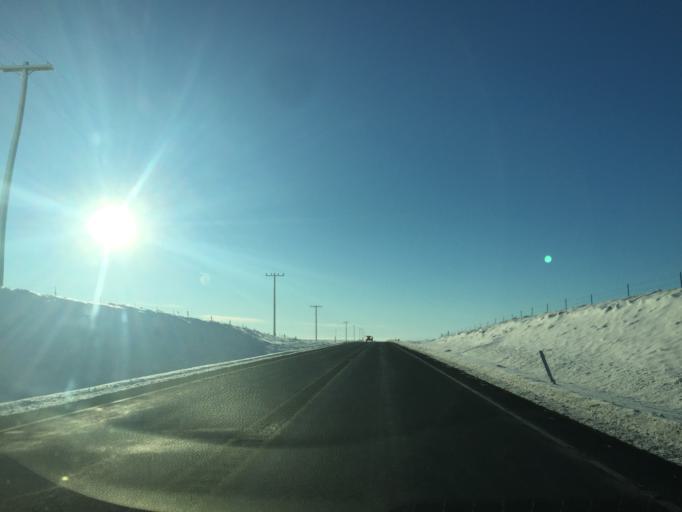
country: US
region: Washington
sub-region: Okanogan County
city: Coulee Dam
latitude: 47.7348
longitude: -118.8563
